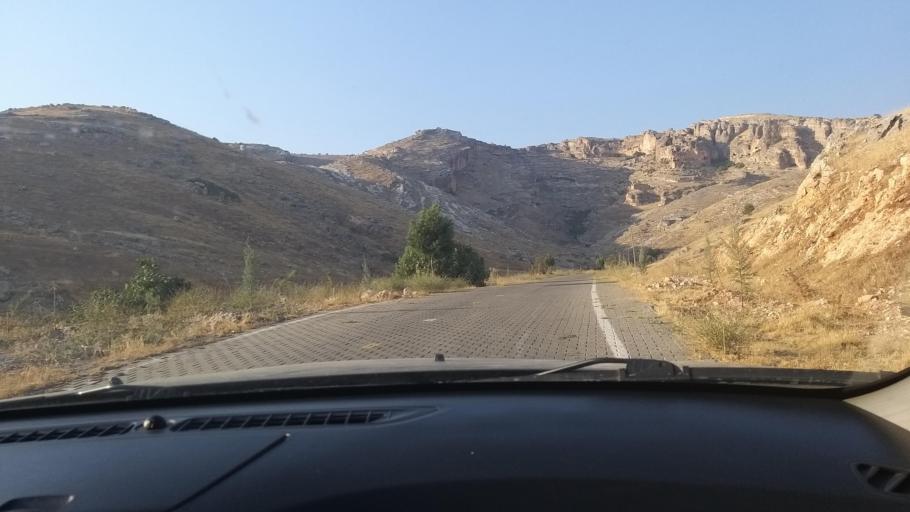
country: TR
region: Diyarbakir
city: Silvan
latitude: 38.1290
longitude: 41.0878
